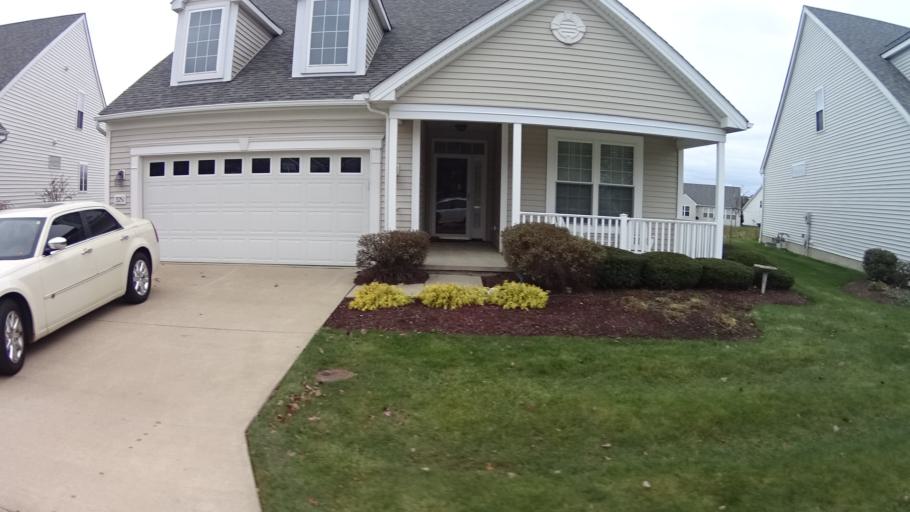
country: US
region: Ohio
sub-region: Lorain County
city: Avon Lake
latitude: 41.4909
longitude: -82.0362
